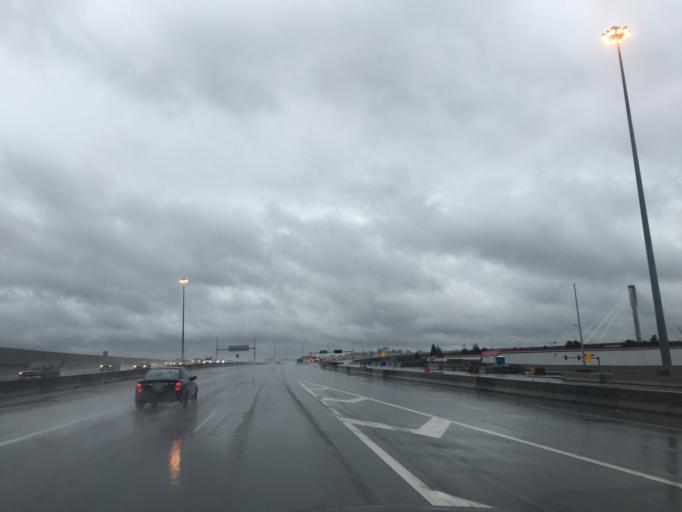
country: CA
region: British Columbia
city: Port Moody
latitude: 49.2282
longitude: -122.8266
